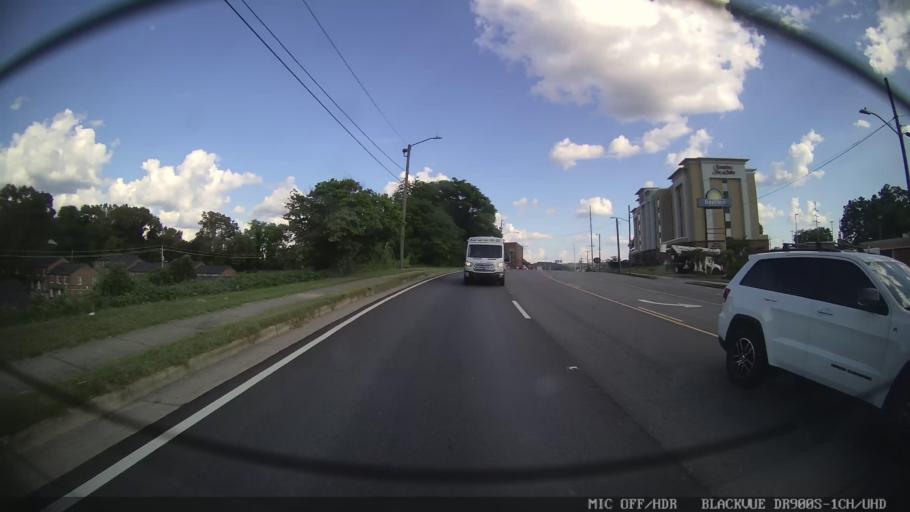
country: US
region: Georgia
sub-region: Floyd County
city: Rome
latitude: 34.2594
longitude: -85.1653
